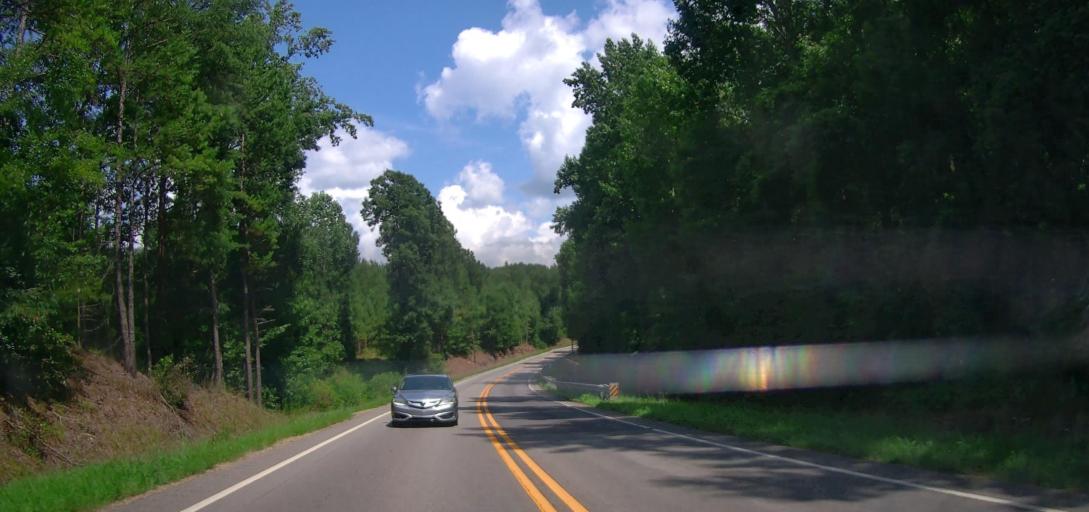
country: US
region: Alabama
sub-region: Cleburne County
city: Heflin
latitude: 33.6412
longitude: -85.4920
